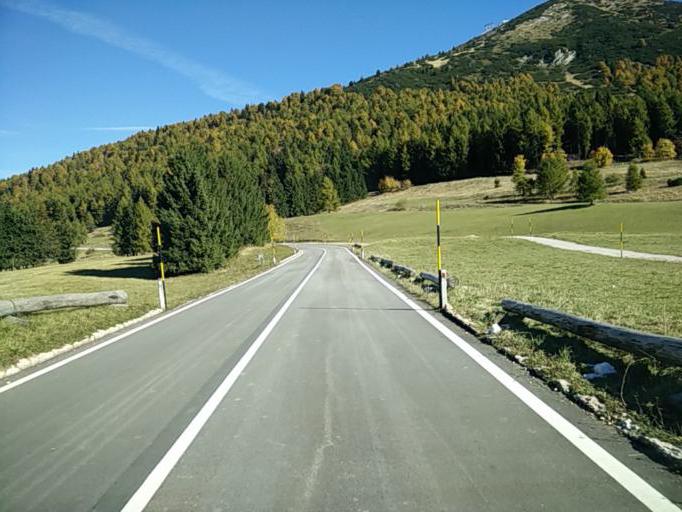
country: IT
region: Trentino-Alto Adige
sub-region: Provincia di Trento
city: Cimoneri
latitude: 46.0224
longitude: 11.0436
